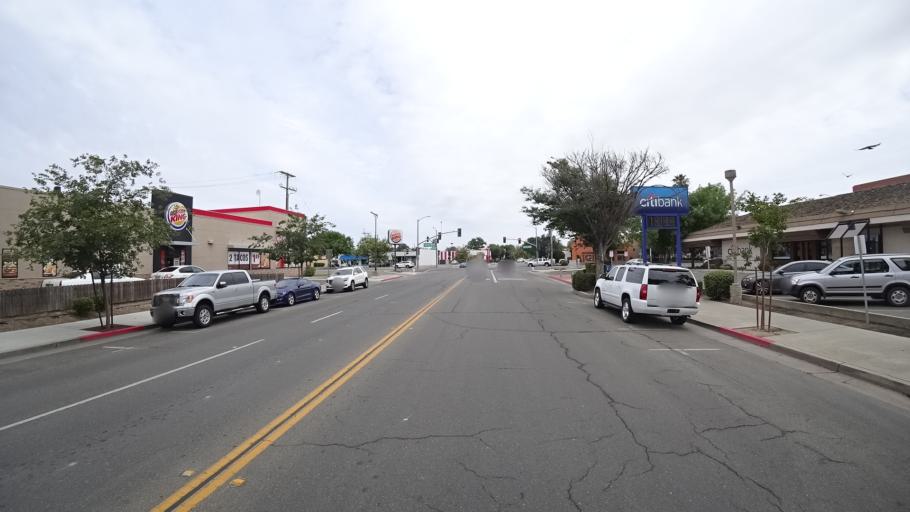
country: US
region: California
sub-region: Kings County
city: Hanford
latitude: 36.3274
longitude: -119.6492
